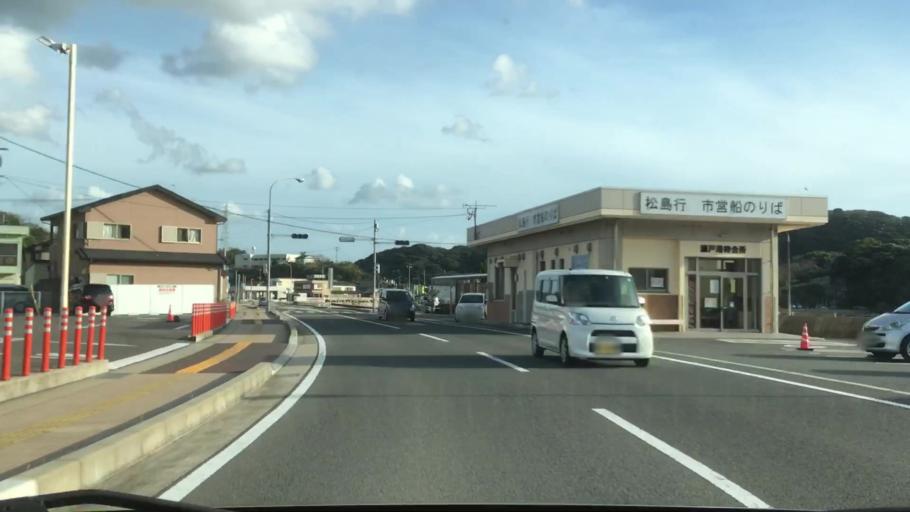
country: JP
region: Nagasaki
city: Togitsu
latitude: 32.9373
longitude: 129.6390
